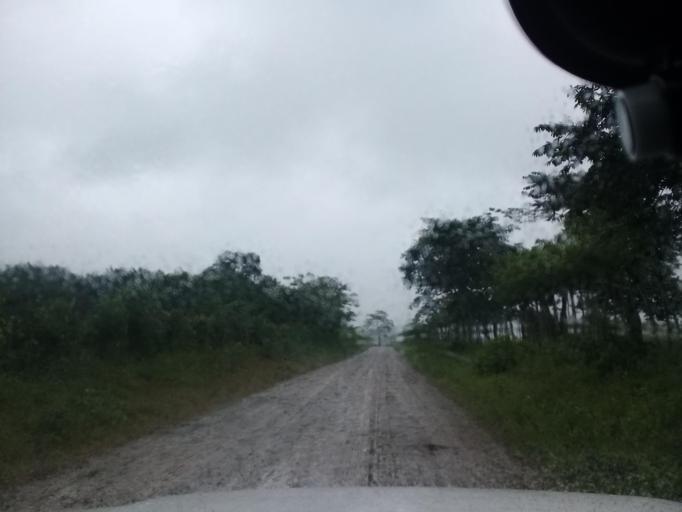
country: MX
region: Veracruz
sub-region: Chalma
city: San Pedro Coyutla
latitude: 21.2449
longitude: -98.4626
